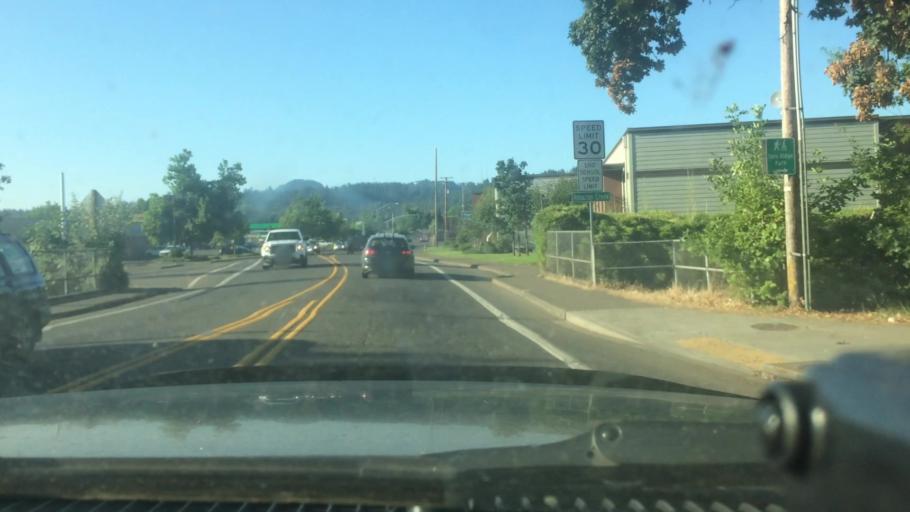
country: US
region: Oregon
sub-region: Lane County
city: Eugene
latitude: 44.0425
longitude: -123.1181
